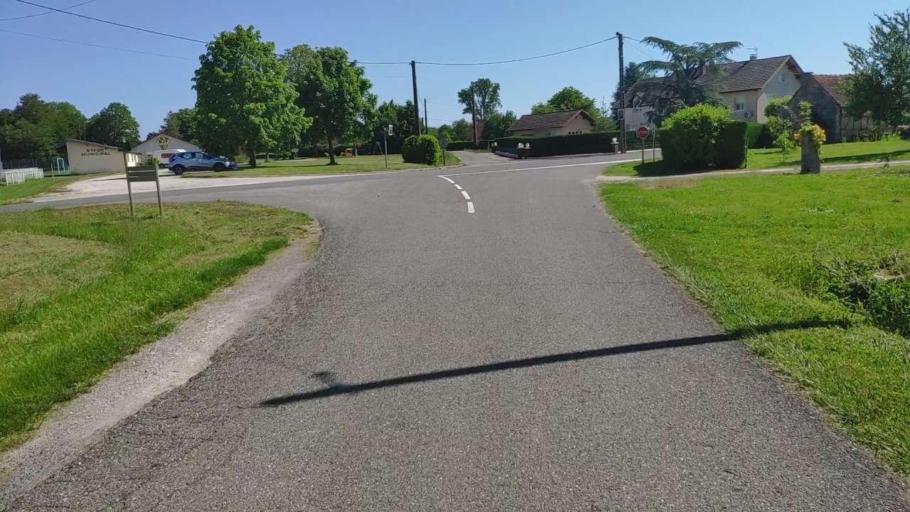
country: FR
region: Franche-Comte
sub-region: Departement du Jura
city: Bletterans
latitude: 46.8031
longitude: 5.4455
